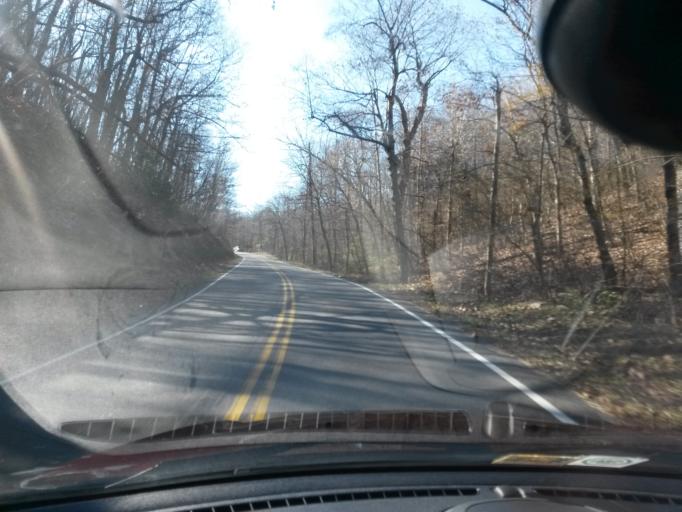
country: US
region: Virginia
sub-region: Botetourt County
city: Buchanan
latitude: 37.4872
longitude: -79.6675
